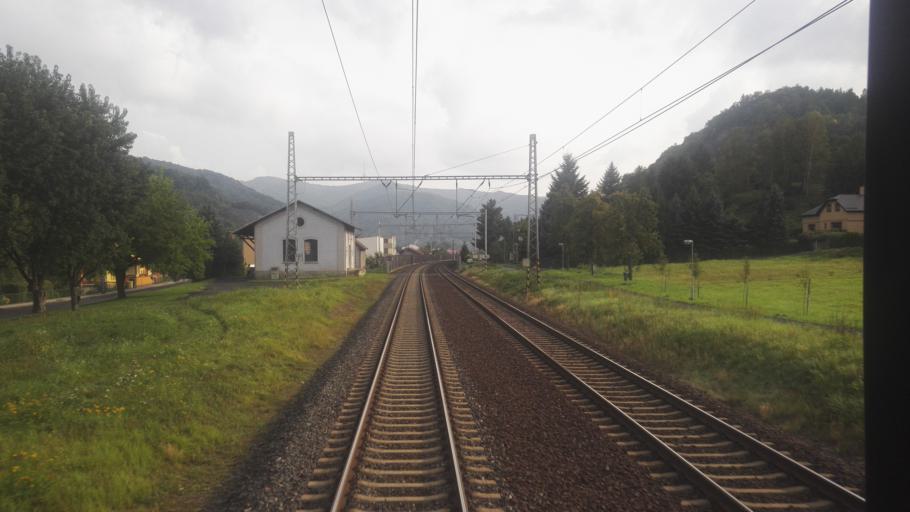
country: CZ
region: Ustecky
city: Povrly
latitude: 50.7155
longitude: 14.1919
